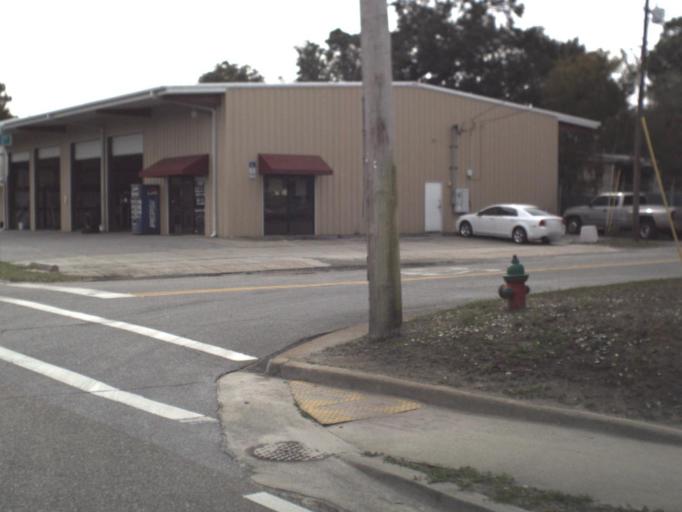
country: US
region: Florida
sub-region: Bay County
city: Panama City
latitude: 30.1644
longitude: -85.6603
